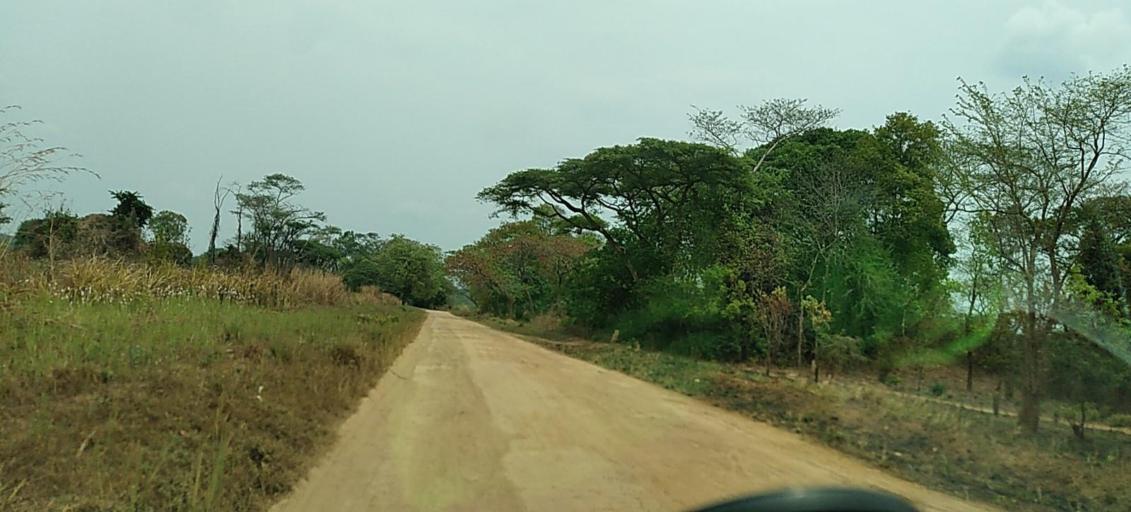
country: ZM
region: North-Western
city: Solwezi
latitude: -12.7893
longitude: 26.5287
